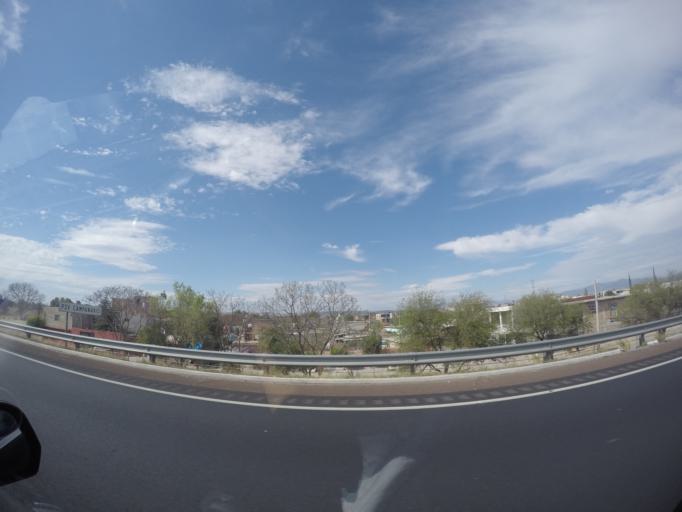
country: MX
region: Guanajuato
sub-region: Celaya
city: Roque
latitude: 20.5579
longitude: -100.8205
